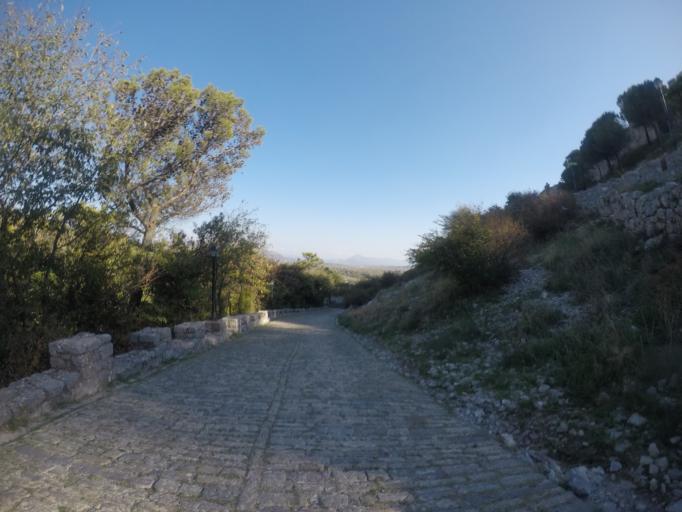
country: AL
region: Shkoder
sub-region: Rrethi i Shkodres
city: Shkoder
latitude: 42.0479
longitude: 19.4951
